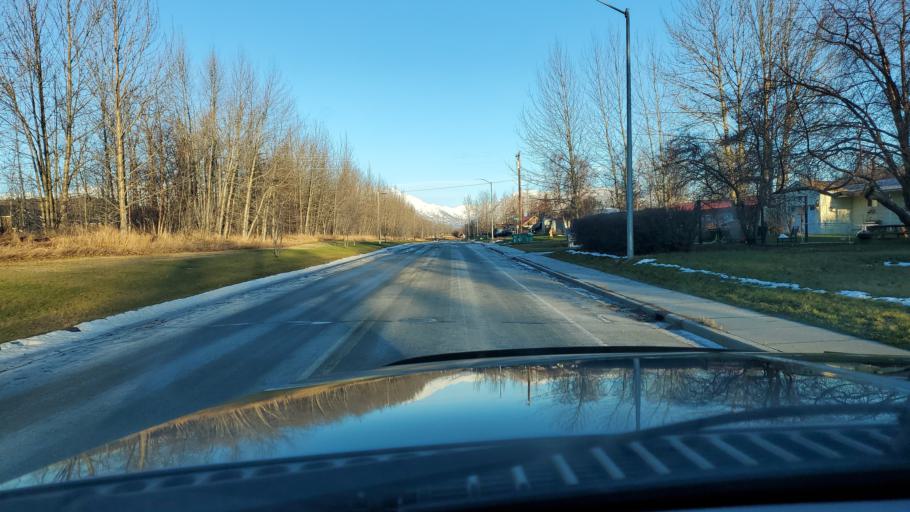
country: US
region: Alaska
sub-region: Matanuska-Susitna Borough
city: Palmer
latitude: 61.6101
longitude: -149.1085
